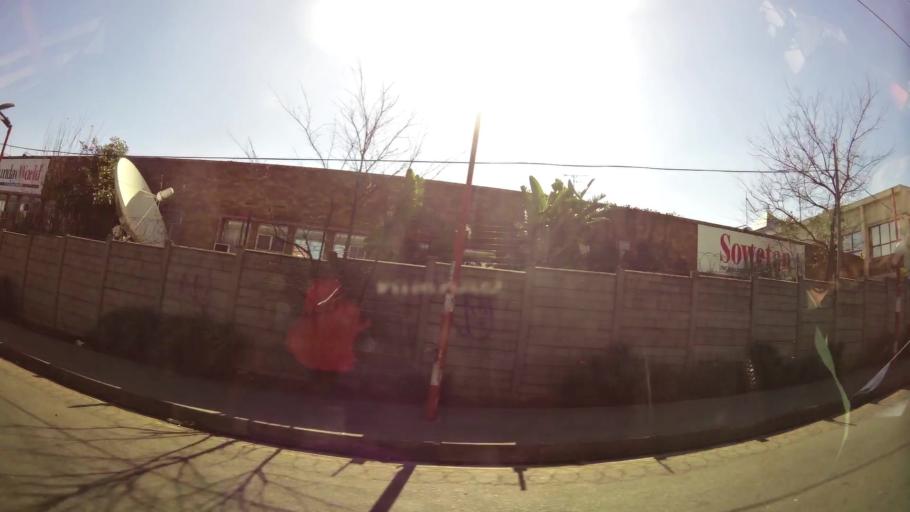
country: ZA
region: Gauteng
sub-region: City of Johannesburg Metropolitan Municipality
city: Johannesburg
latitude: -26.1901
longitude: 27.9678
